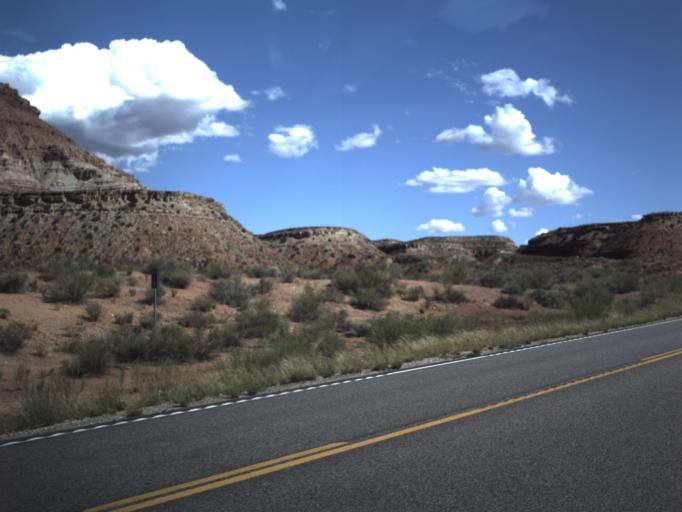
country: US
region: Utah
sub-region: Washington County
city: Hurricane
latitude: 37.1439
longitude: -113.2537
